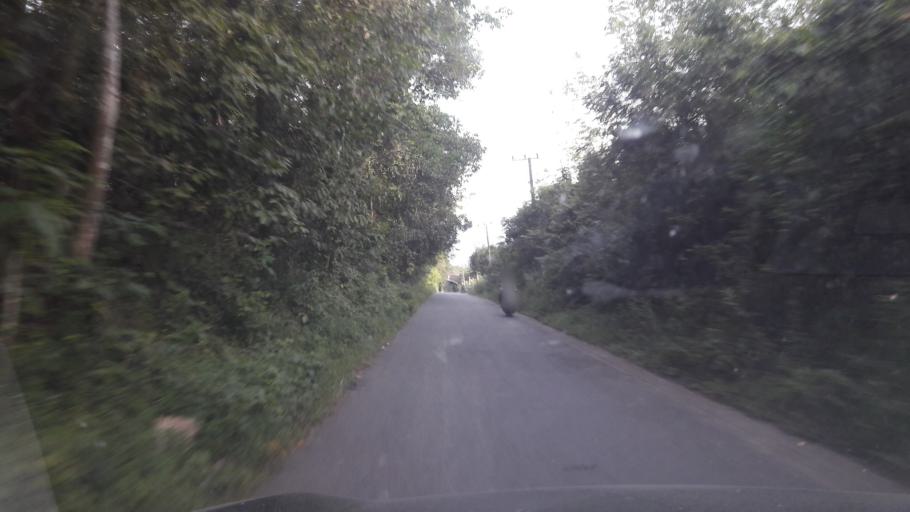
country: ID
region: South Sumatra
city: Gunungmenang
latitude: -3.2975
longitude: 104.0872
